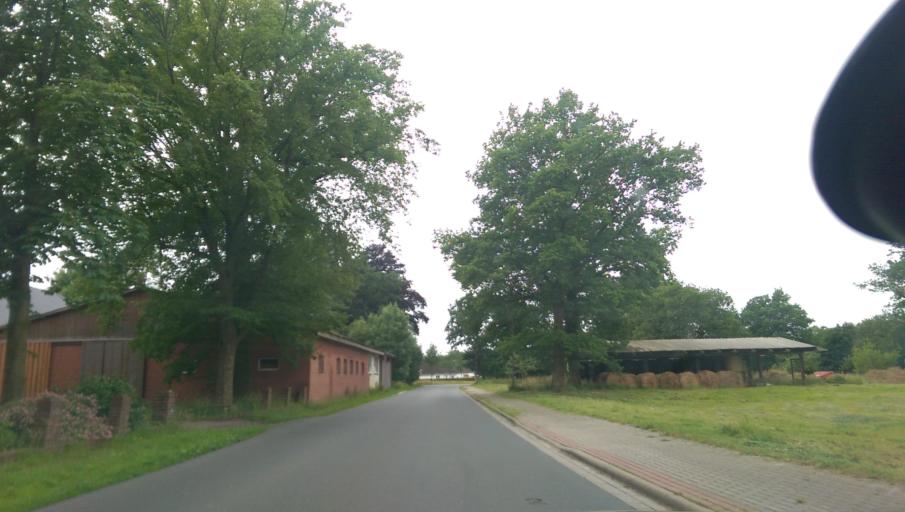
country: DE
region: Lower Saxony
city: Gyhum
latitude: 53.1784
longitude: 9.2870
